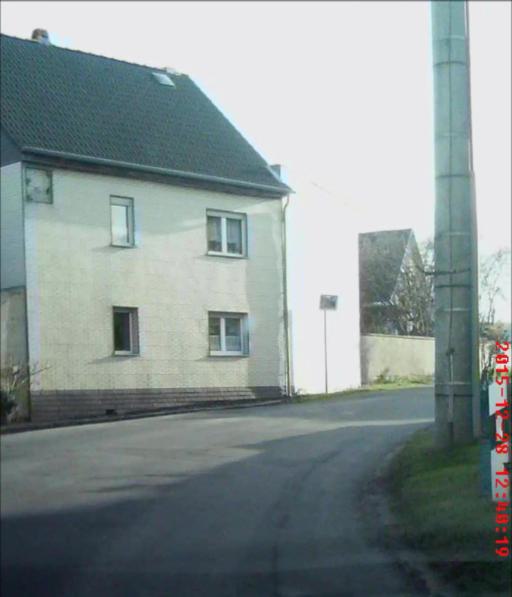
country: DE
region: Thuringia
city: Ossmanstedt
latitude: 51.0105
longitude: 11.4242
